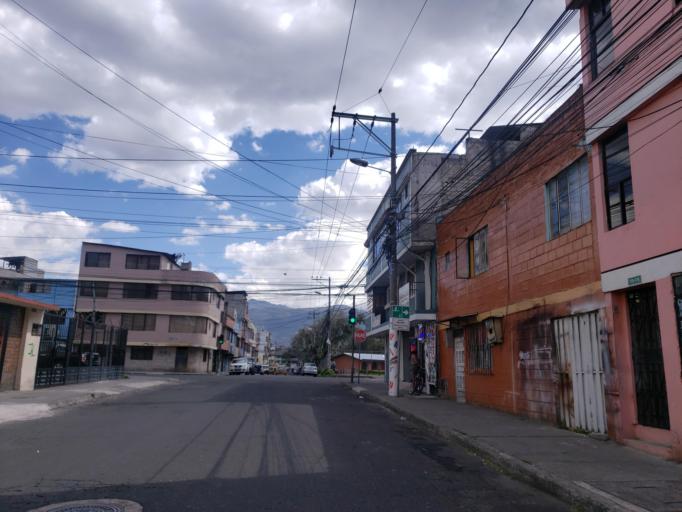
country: EC
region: Pichincha
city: Quito
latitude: -0.2701
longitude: -78.5371
